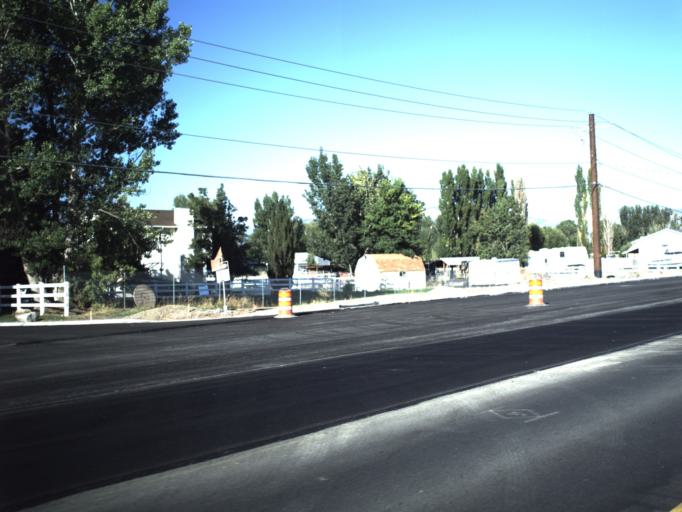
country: US
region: Utah
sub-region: Weber County
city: West Haven
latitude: 41.1907
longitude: -112.0803
